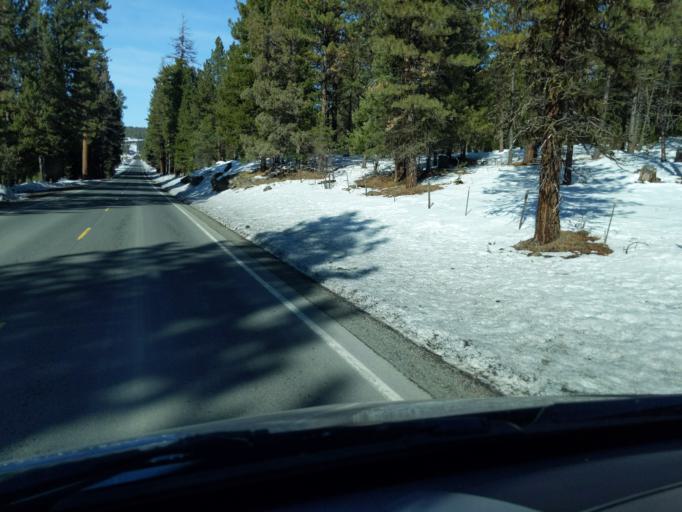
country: US
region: Oregon
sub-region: Grant County
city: John Day
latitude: 44.9204
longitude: -119.0097
